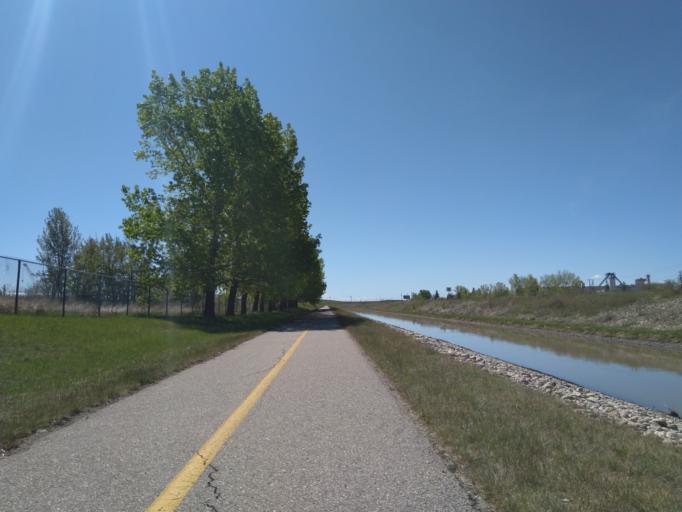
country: CA
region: Alberta
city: Calgary
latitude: 50.9720
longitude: -113.9887
